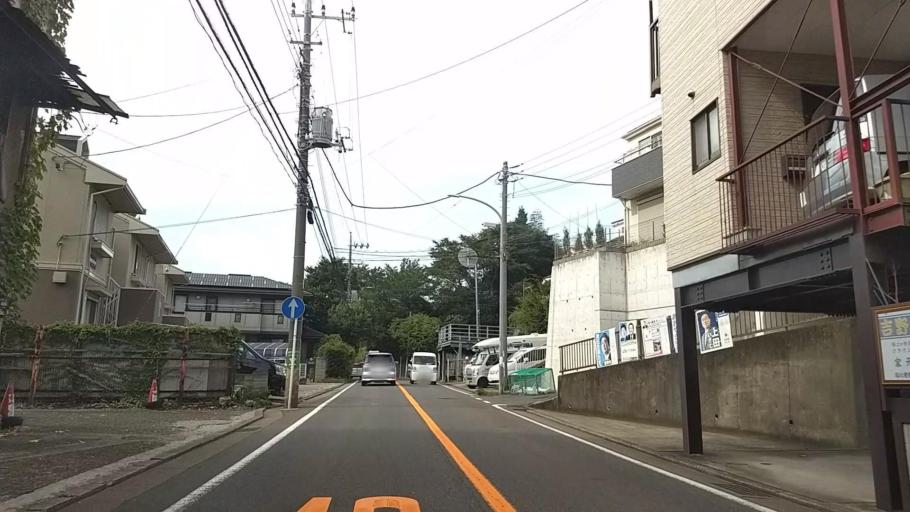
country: JP
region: Kanagawa
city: Yokohama
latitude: 35.4883
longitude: 139.5724
